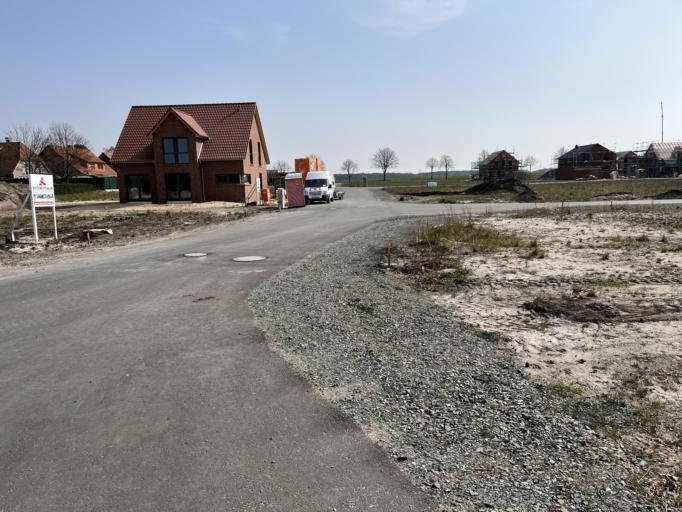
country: DE
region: Lower Saxony
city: Isernhagen Farster Bauerschaft
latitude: 52.5073
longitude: 9.8738
